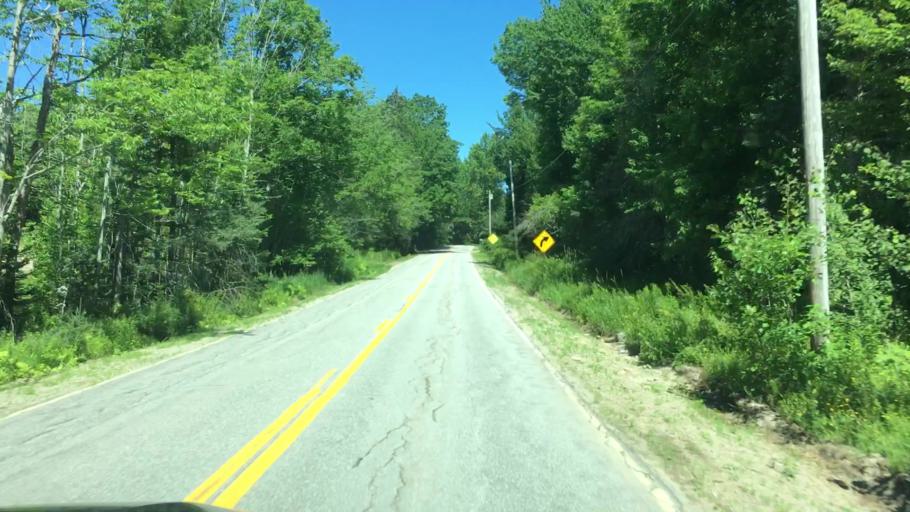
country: US
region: Maine
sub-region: Hancock County
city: Penobscot
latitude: 44.4264
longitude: -68.7110
